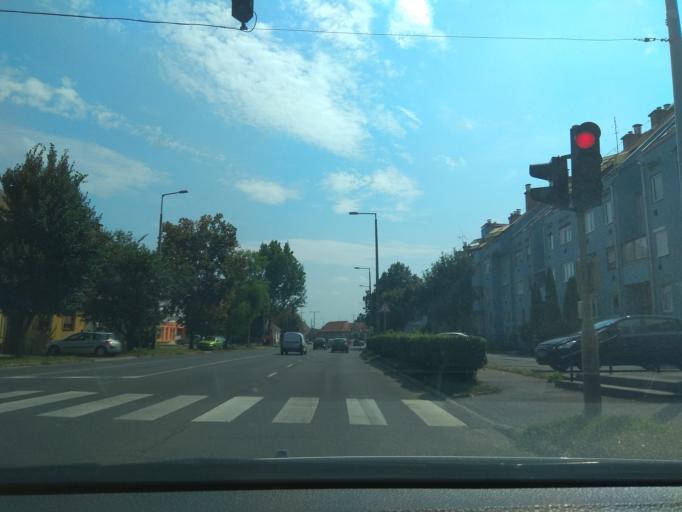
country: HU
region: Heves
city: Eger
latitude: 47.8946
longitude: 20.3697
